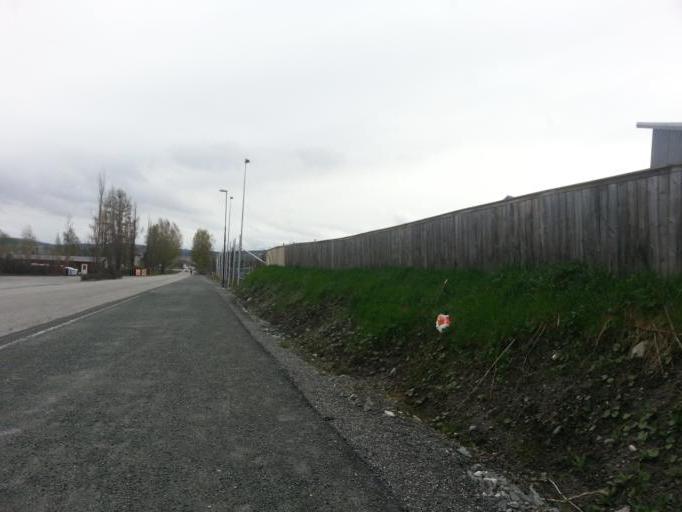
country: NO
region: Nord-Trondelag
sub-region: Levanger
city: Skogn
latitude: 63.7020
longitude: 11.1946
